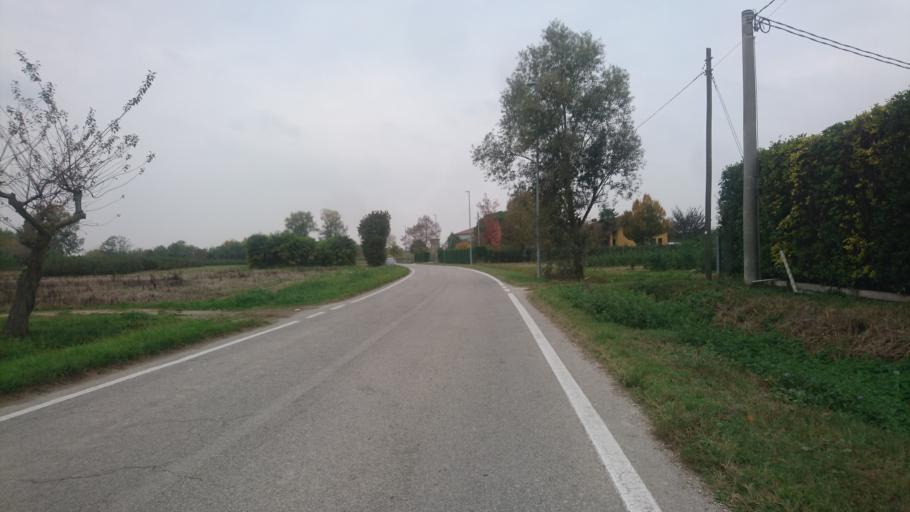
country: IT
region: Veneto
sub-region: Provincia di Venezia
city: Tombelle
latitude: 45.3878
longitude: 11.9806
